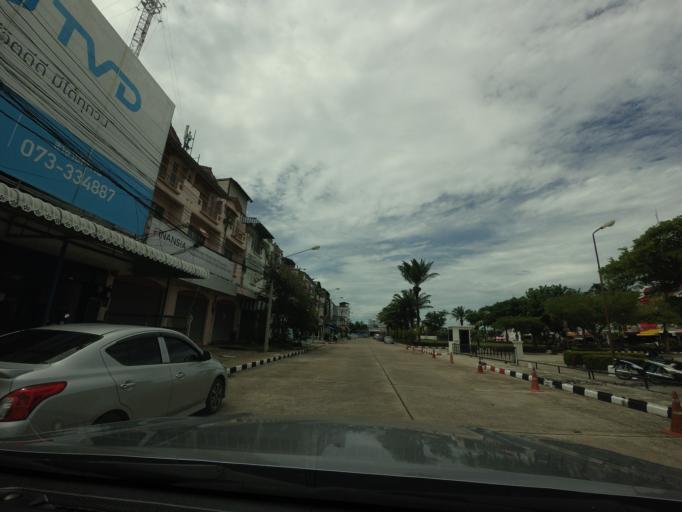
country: TH
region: Pattani
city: Pattani
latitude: 6.8635
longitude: 101.2341
